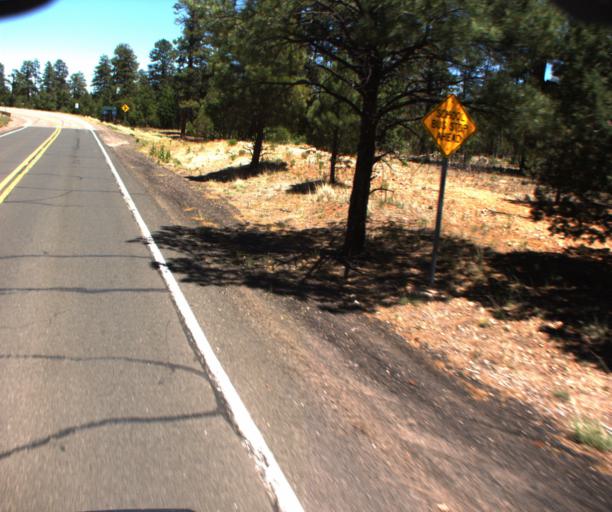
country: US
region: Arizona
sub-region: Gila County
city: Star Valley
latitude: 34.6317
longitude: -111.1126
